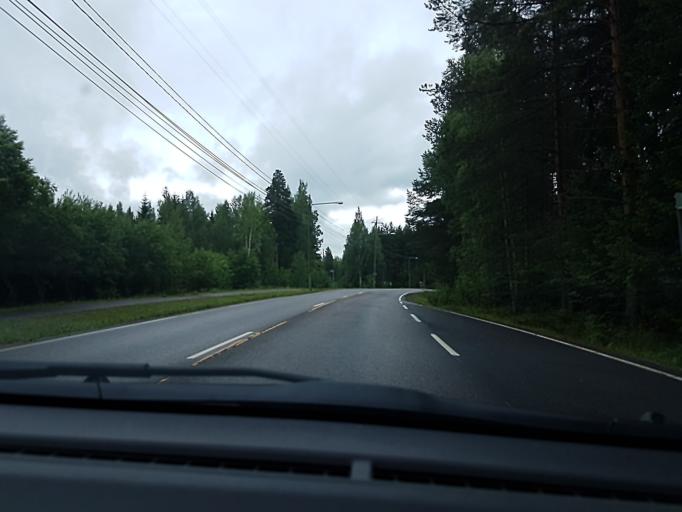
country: FI
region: Uusimaa
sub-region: Helsinki
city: Pornainen
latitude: 60.4657
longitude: 25.3894
